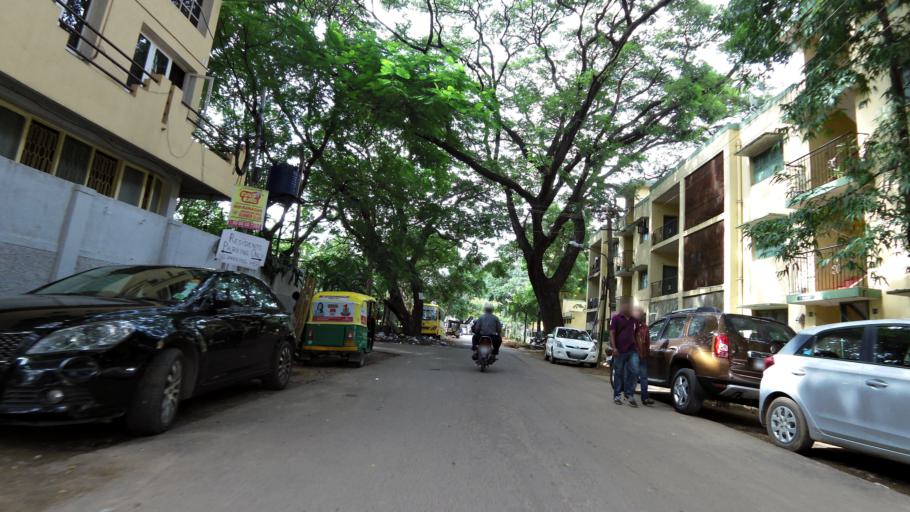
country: IN
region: Karnataka
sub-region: Bangalore Urban
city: Bangalore
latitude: 12.9708
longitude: 77.6387
